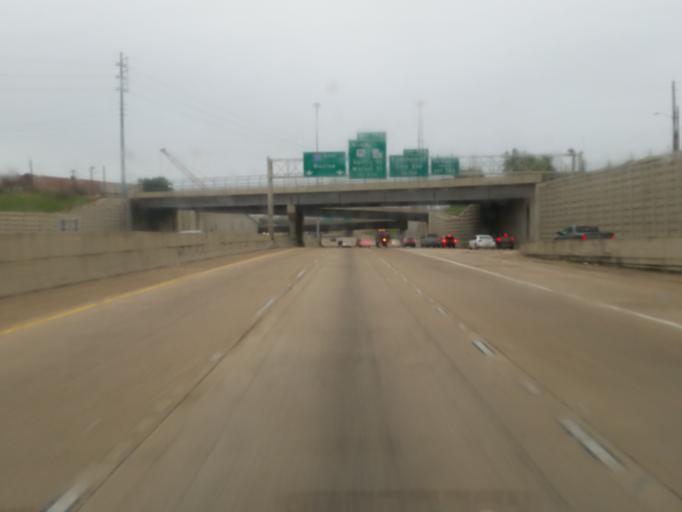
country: US
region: Louisiana
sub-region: Caddo Parish
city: Shreveport
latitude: 32.4980
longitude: -93.7560
